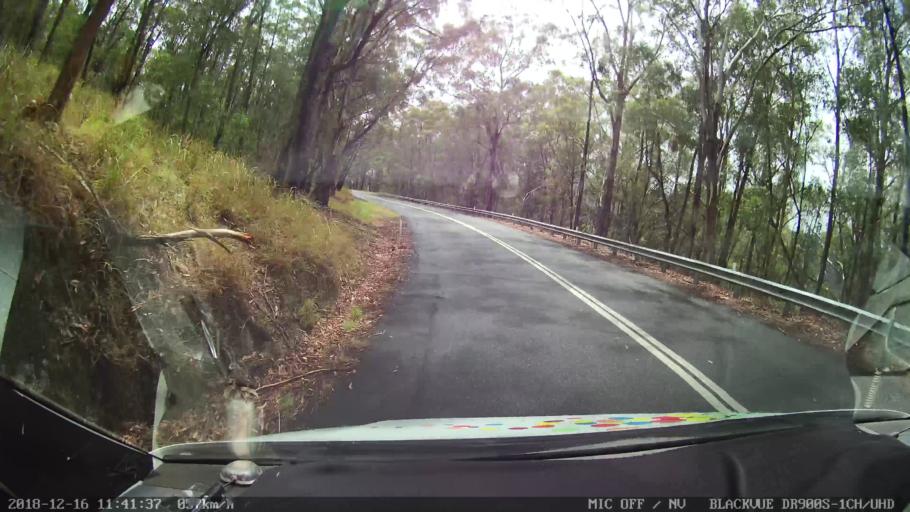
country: AU
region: New South Wales
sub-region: Tenterfield Municipality
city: Carrolls Creek
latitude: -28.9585
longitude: 152.2110
